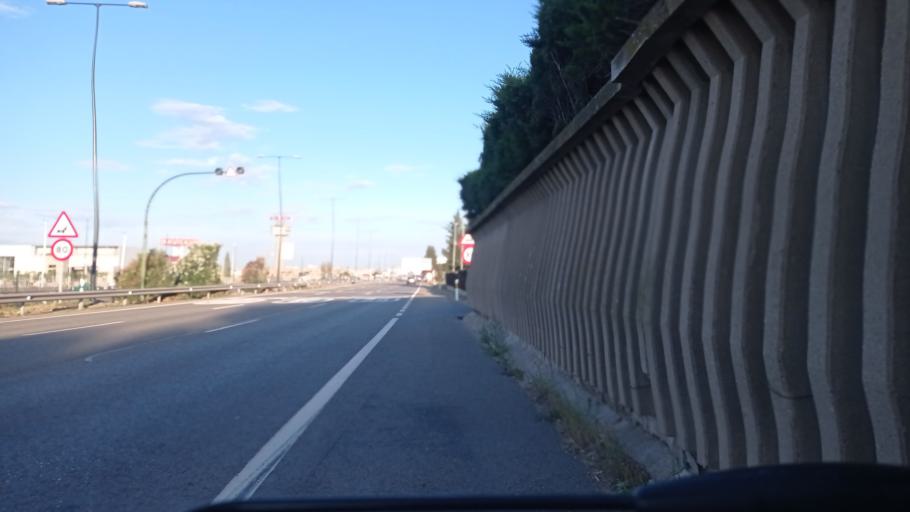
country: ES
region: Aragon
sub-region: Provincia de Zaragoza
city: Oliver-Valdefierro, Oliver, Valdefierro
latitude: 41.6757
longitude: -0.9566
